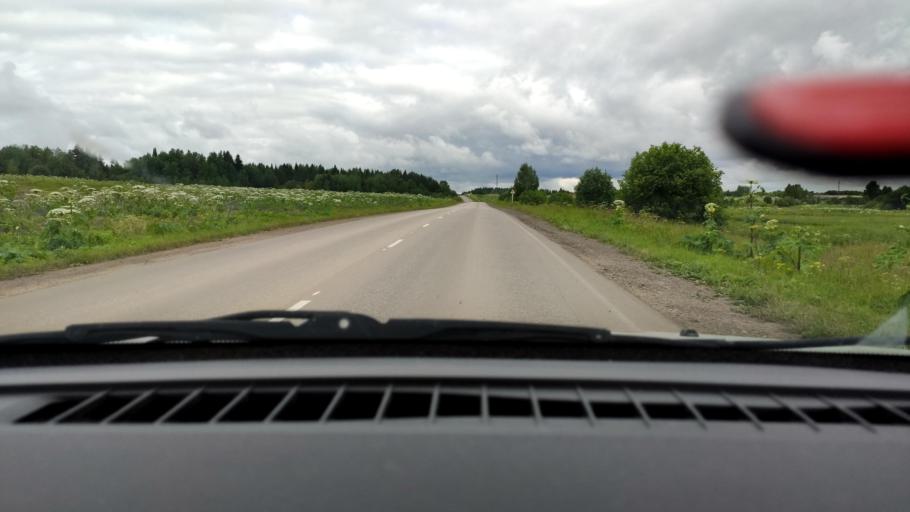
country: RU
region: Perm
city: Chaykovskaya
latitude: 58.1209
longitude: 55.5681
